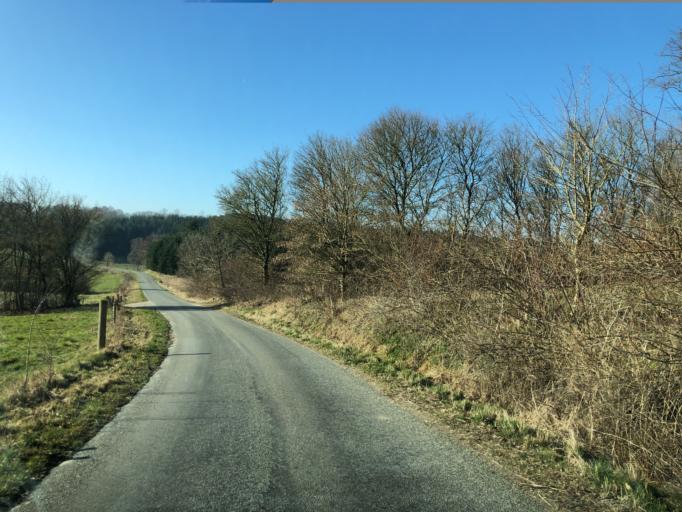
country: DK
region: Central Jutland
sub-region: Favrskov Kommune
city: Hammel
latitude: 56.1979
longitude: 9.7820
